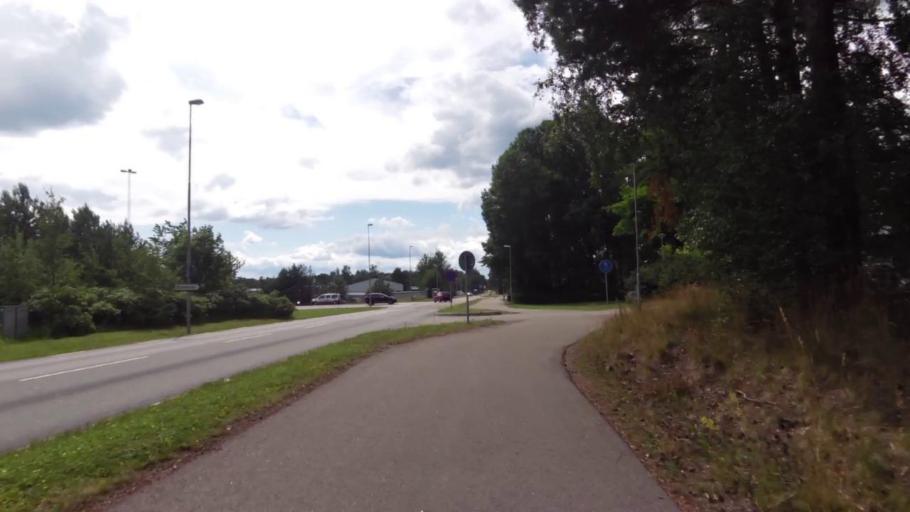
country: SE
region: OEstergoetland
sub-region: Linkopings Kommun
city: Malmslatt
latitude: 58.4012
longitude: 15.5521
